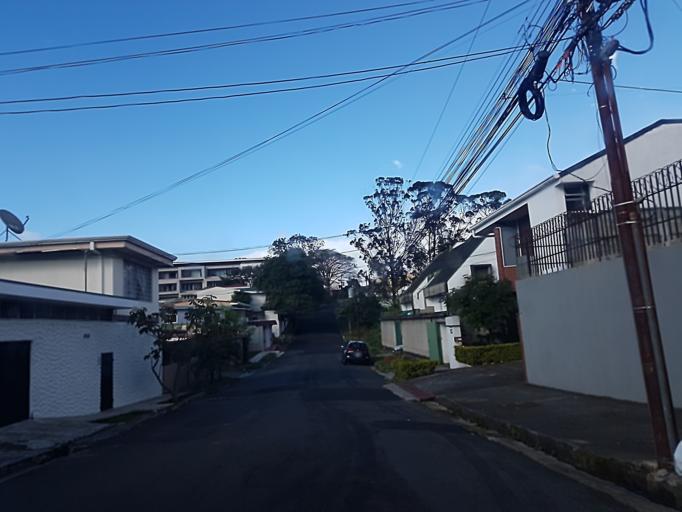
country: CR
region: San Jose
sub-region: Canton de Goicoechea
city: Guadalupe
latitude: 9.9367
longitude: -84.0604
